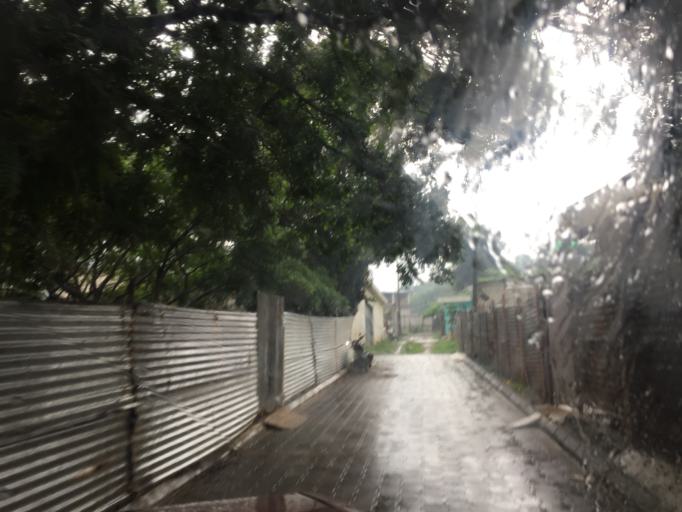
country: GT
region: Guatemala
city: Amatitlan
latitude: 14.5006
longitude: -90.6457
